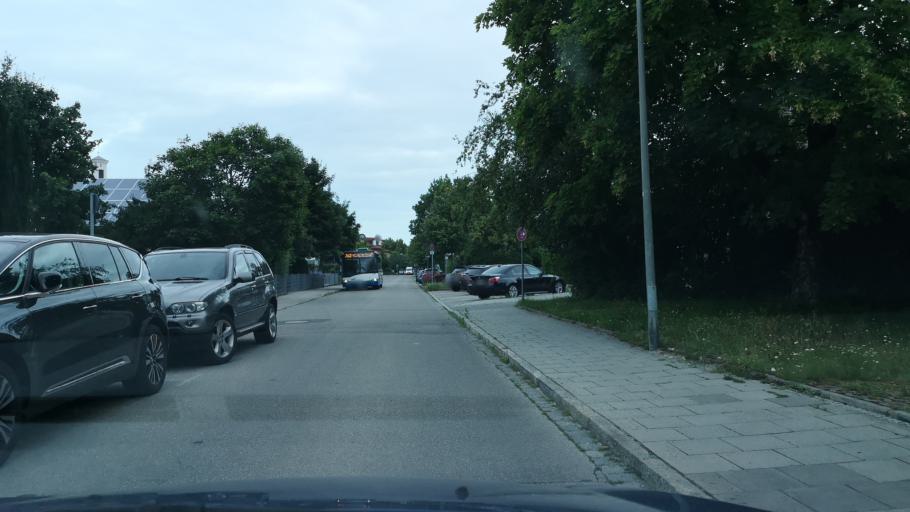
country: DE
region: Bavaria
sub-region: Upper Bavaria
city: Kirchheim bei Muenchen
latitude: 48.1606
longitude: 11.7611
